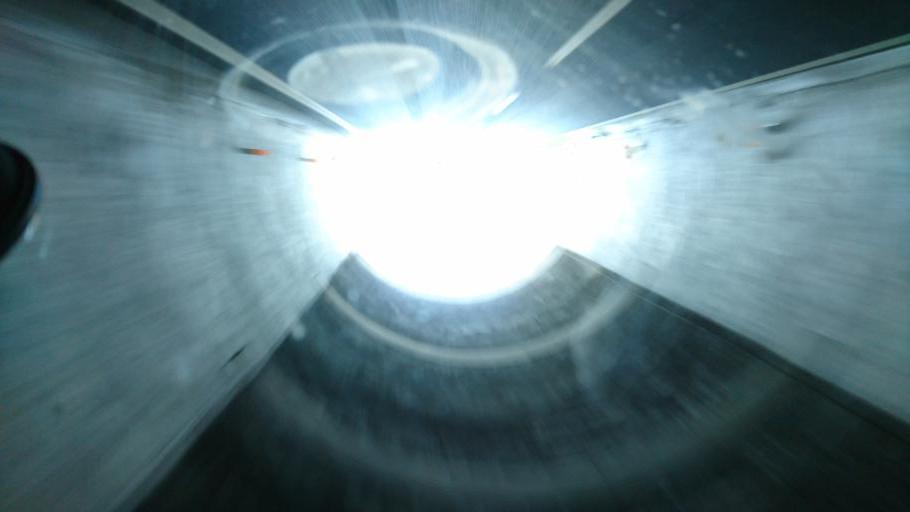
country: IT
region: Liguria
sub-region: Provincia di Savona
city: Valleggia
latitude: 44.3013
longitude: 8.4475
